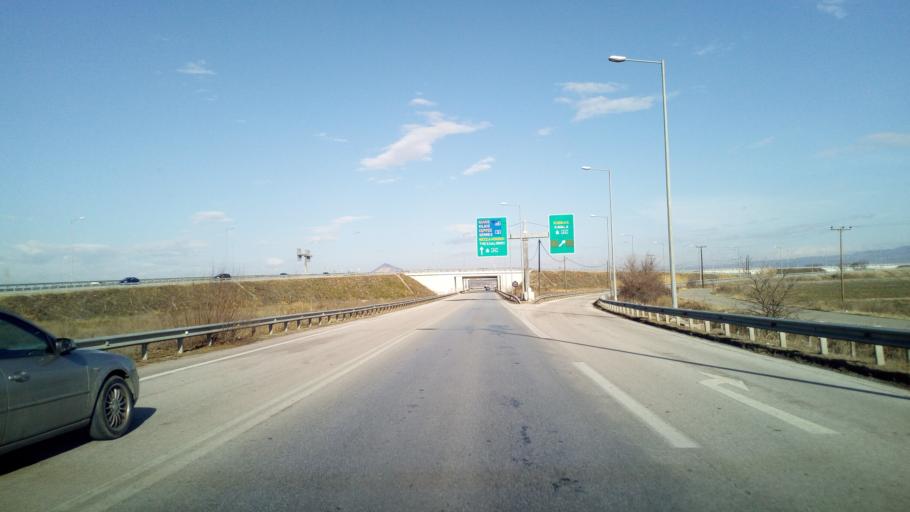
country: GR
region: Central Macedonia
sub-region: Nomos Thessalonikis
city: Lagyna
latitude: 40.7351
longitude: 23.0122
